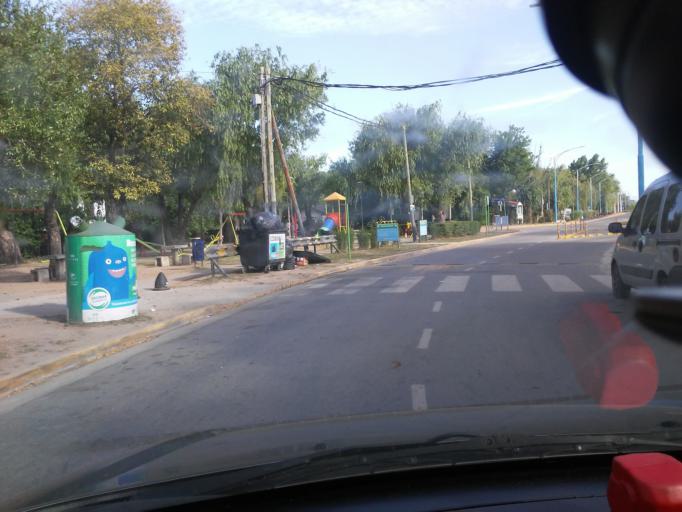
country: AR
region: Buenos Aires
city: Belen de Escobar
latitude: -34.2471
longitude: -58.7311
